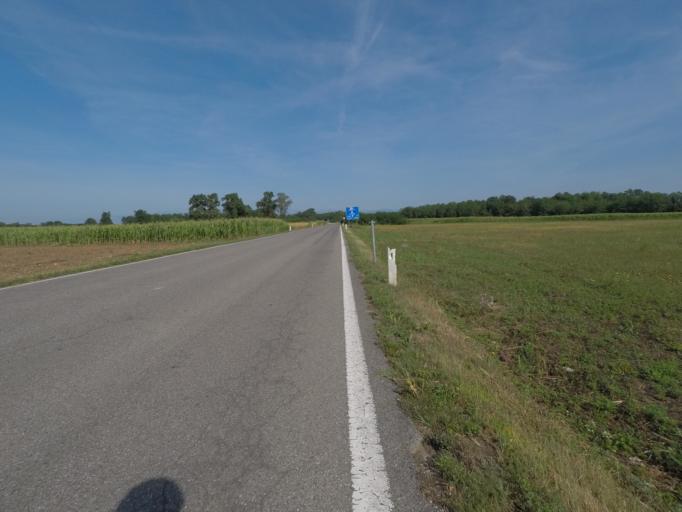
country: IT
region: Friuli Venezia Giulia
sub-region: Provincia di Udine
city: Colloredo di Prato
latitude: 46.0559
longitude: 13.1198
